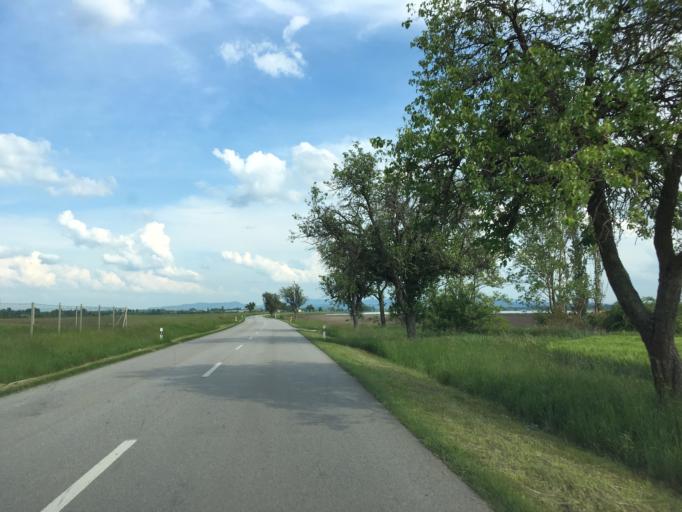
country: HU
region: Komarom-Esztergom
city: Almasfuzito
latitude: 47.7975
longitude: 18.2465
